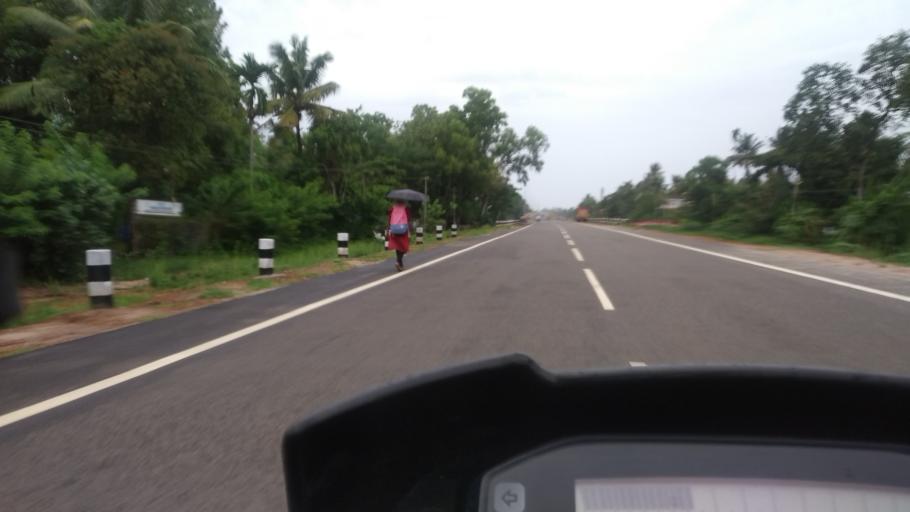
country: IN
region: Kerala
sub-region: Alappuzha
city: Alleppey
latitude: 9.5084
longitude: 76.3242
